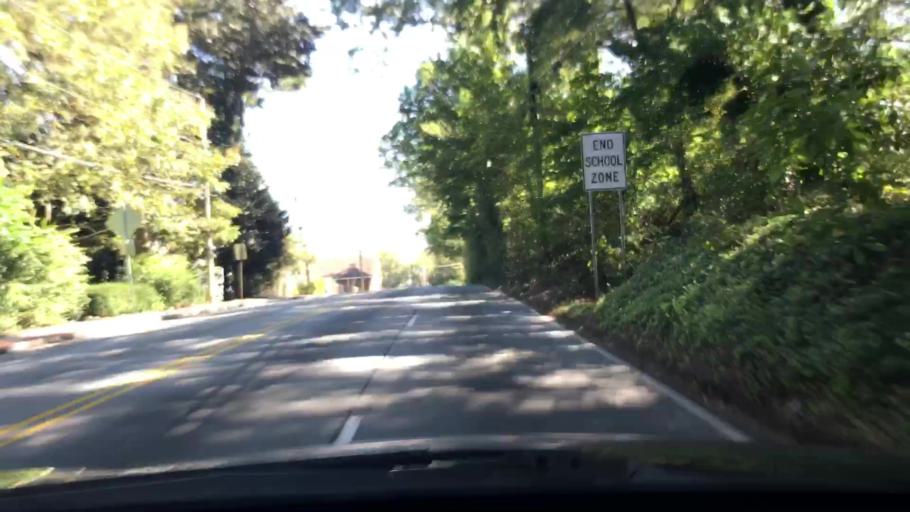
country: US
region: Georgia
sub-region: DeKalb County
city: Decatur
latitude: 33.7473
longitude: -84.3129
